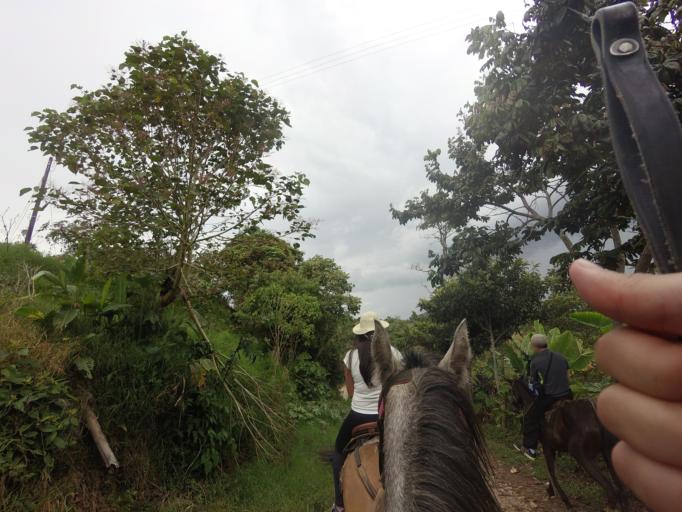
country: CO
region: Huila
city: San Agustin
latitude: 1.8920
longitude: -76.2952
